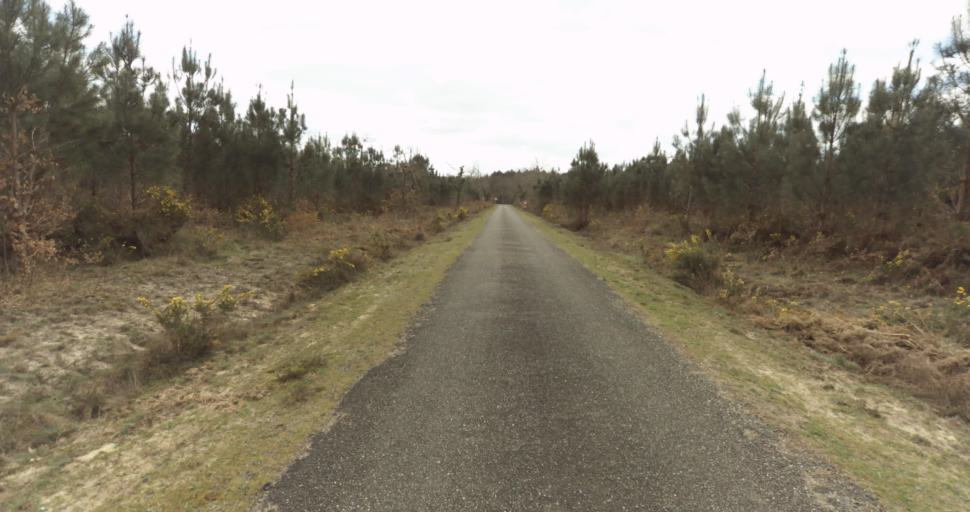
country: FR
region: Aquitaine
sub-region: Departement des Landes
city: Roquefort
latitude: 44.0787
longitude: -0.4403
